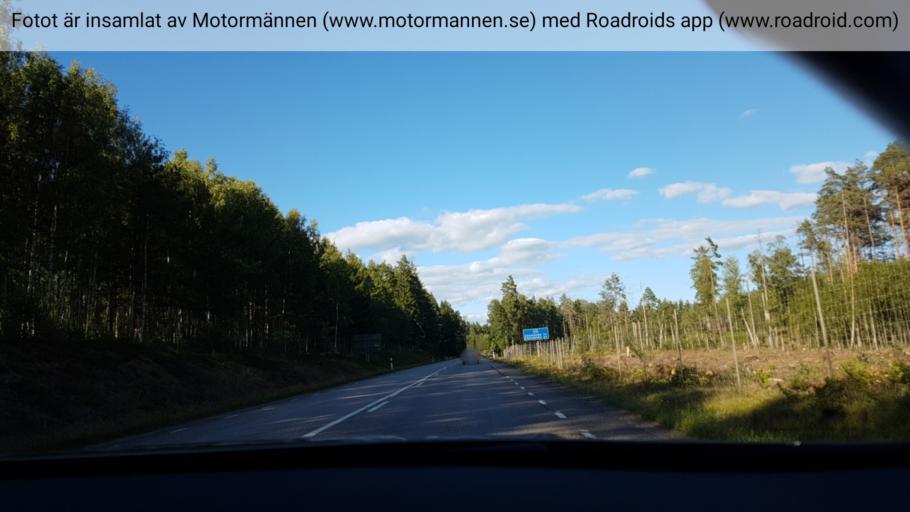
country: SE
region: Vaestra Goetaland
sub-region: Tibro Kommun
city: Tibro
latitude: 58.4463
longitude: 14.1896
